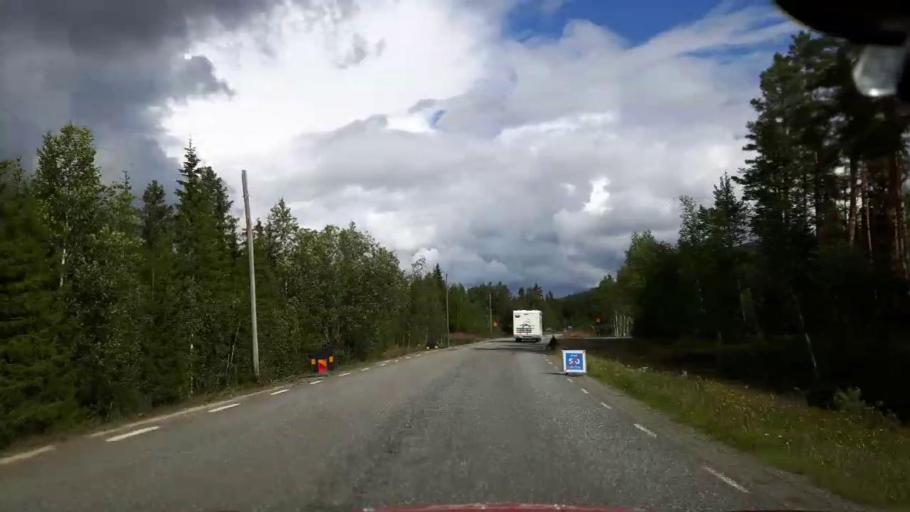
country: SE
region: Vaesterbotten
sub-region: Vilhelmina Kommun
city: Sjoberg
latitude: 64.9350
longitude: 15.8578
